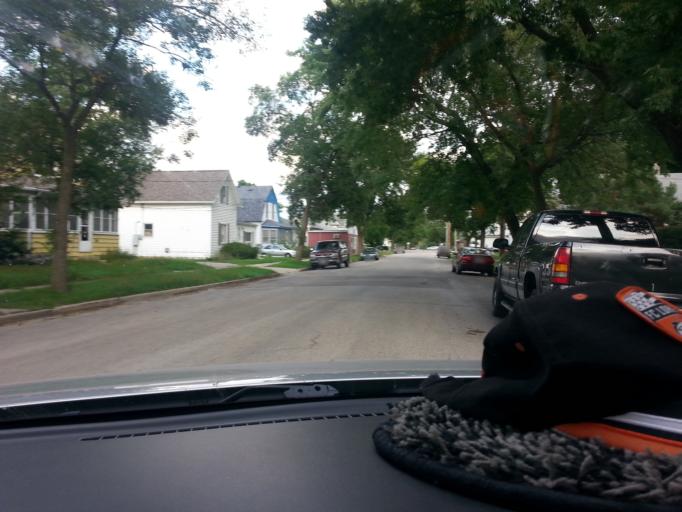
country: US
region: Minnesota
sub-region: Olmsted County
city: Rochester
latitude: 44.0332
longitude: -92.4655
